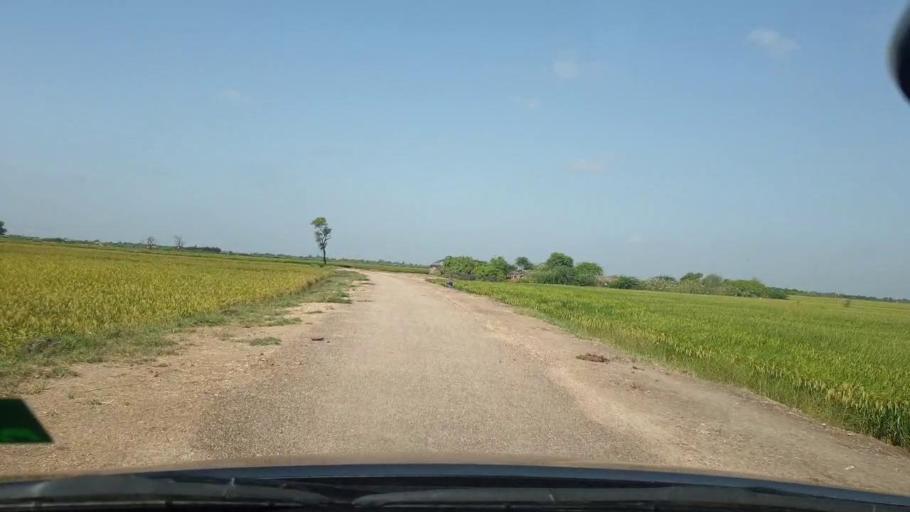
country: PK
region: Sindh
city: Tando Bago
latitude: 24.7449
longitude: 68.9720
